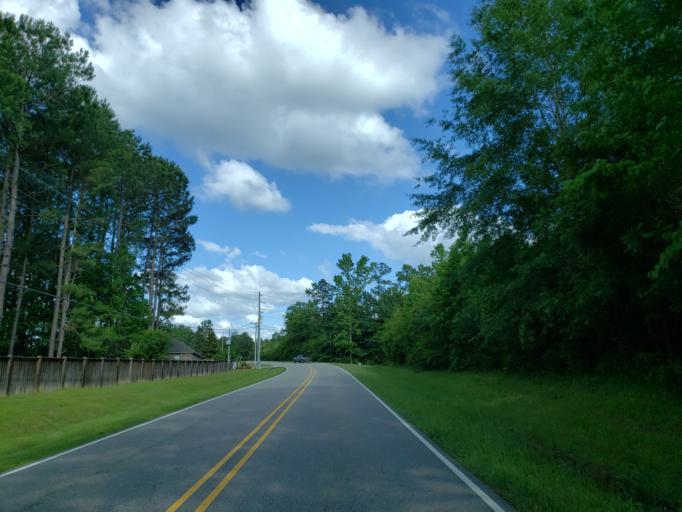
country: US
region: Mississippi
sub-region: Lamar County
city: West Hattiesburg
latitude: 31.2890
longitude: -89.4471
